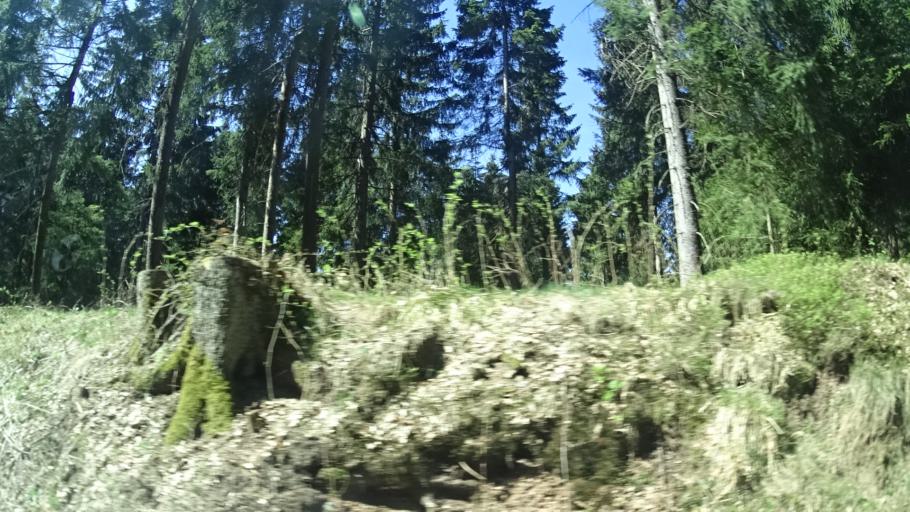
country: DE
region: Thuringia
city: Frauenwald
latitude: 50.5488
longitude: 10.8597
